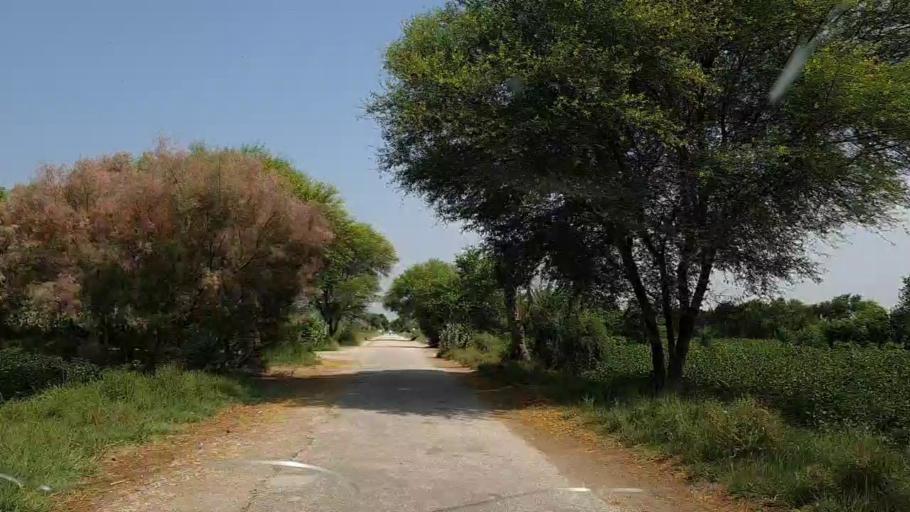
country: PK
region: Sindh
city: Adilpur
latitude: 27.8299
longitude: 69.2929
